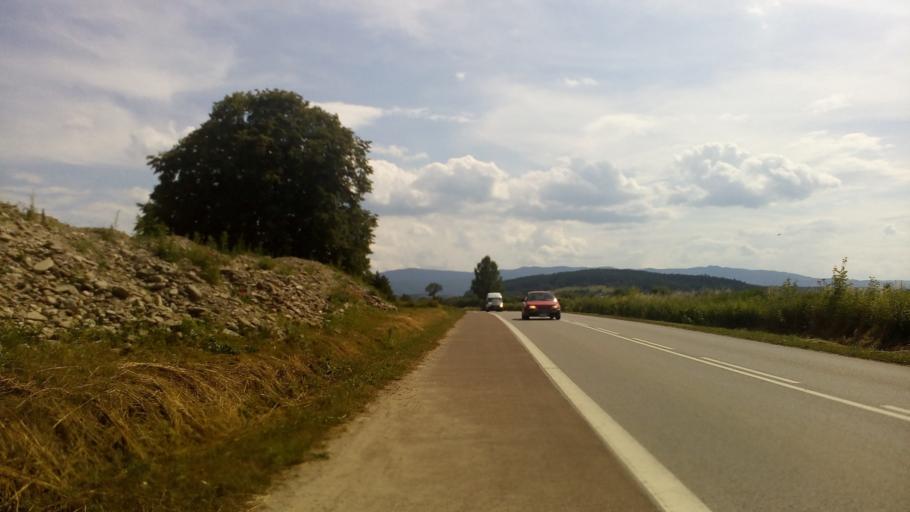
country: PL
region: Lesser Poland Voivodeship
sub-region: Powiat nowosadecki
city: Stary Sacz
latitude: 49.5783
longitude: 20.6369
